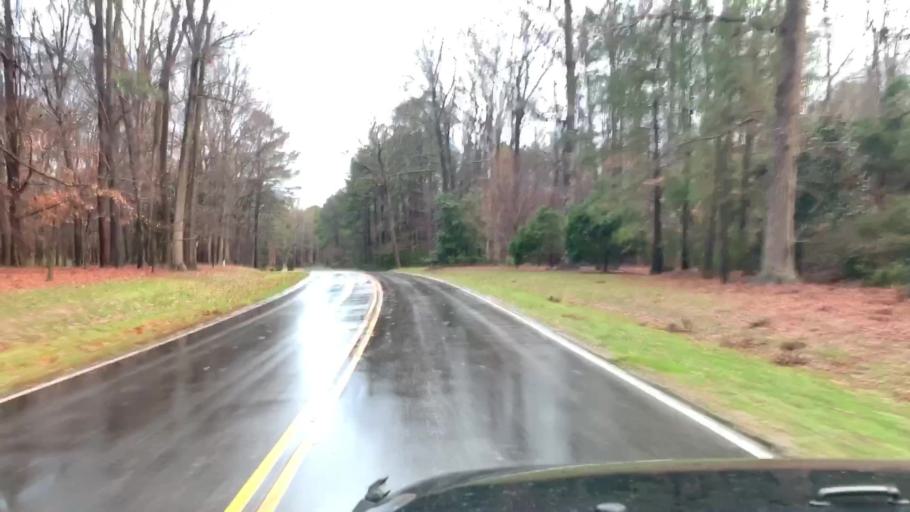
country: US
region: Virginia
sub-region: City of Williamsburg
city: Williamsburg
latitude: 37.2369
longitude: -76.6598
